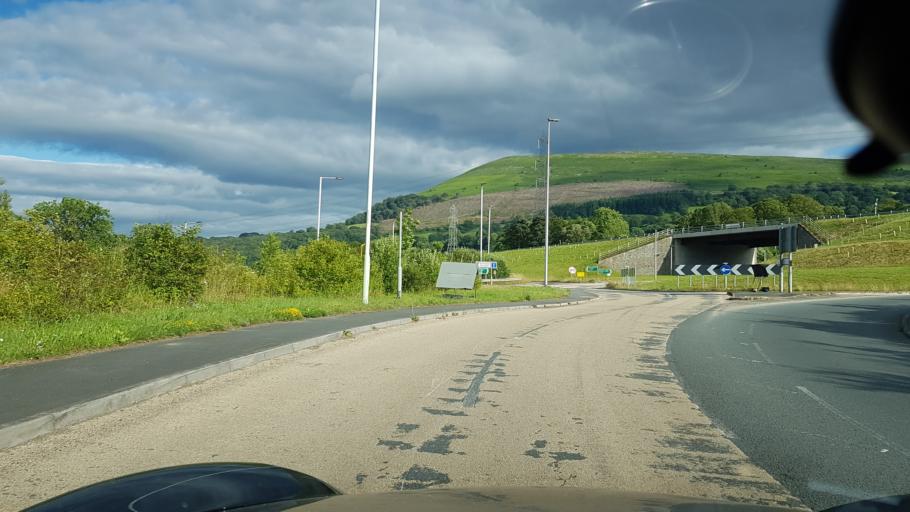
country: GB
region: Wales
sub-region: Monmouthshire
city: Gilwern
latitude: 51.8240
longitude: -3.0765
